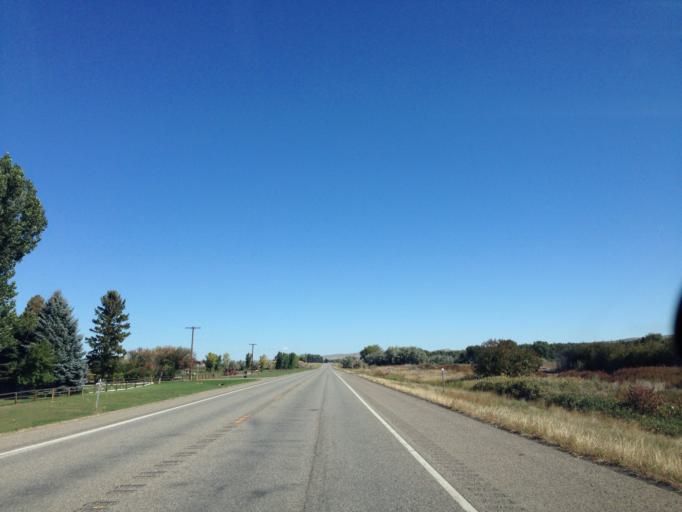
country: US
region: Montana
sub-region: Yellowstone County
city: Laurel
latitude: 45.4181
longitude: -108.8851
